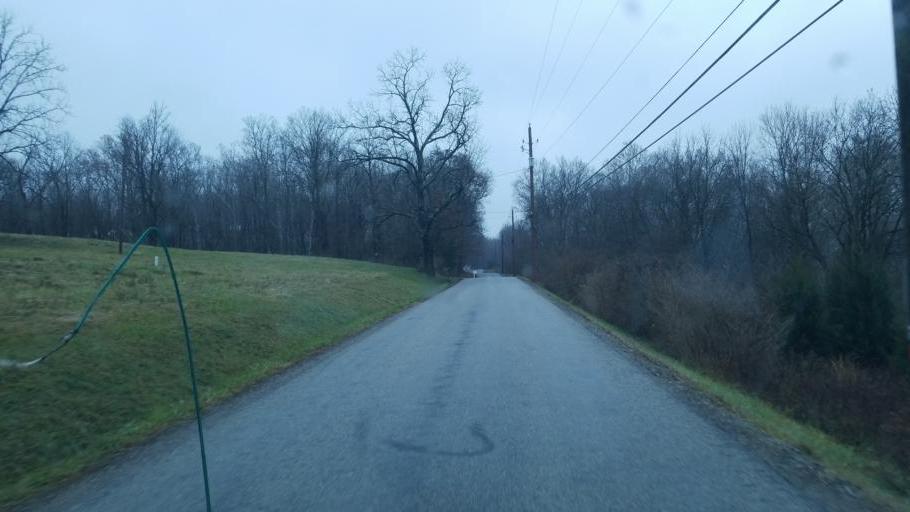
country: US
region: Ohio
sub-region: Delaware County
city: Lewis Center
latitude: 40.1938
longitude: -83.0497
